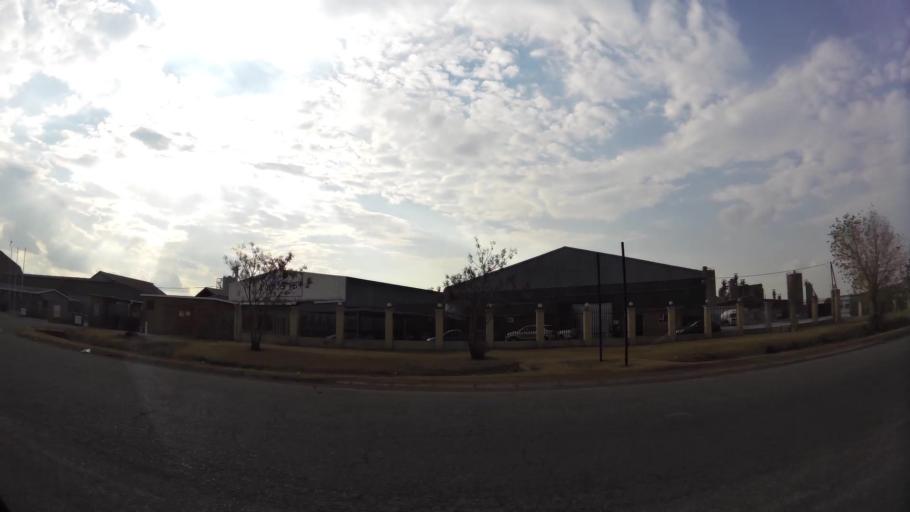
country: ZA
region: Gauteng
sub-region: Sedibeng District Municipality
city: Vereeniging
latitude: -26.6848
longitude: 27.9084
